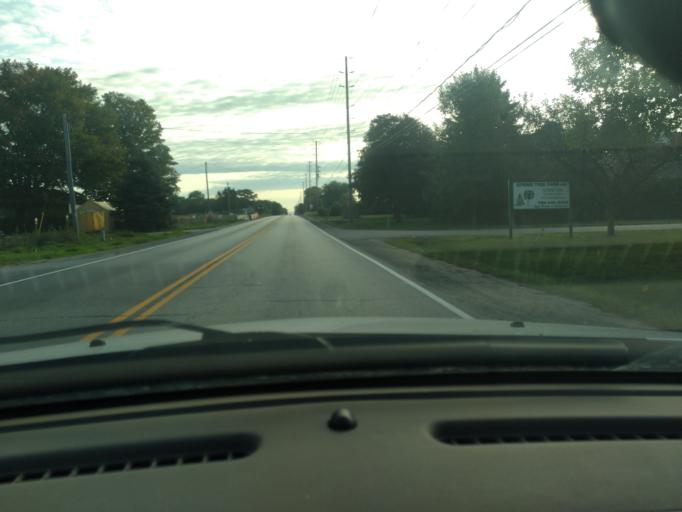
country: CA
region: Ontario
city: Innisfil
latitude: 44.3032
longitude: -79.5996
